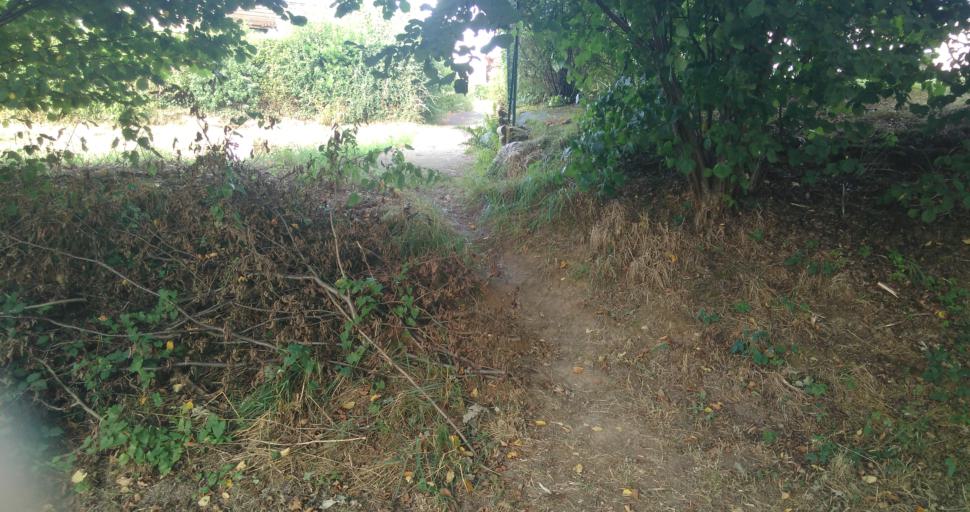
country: FR
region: Brittany
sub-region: Departement d'Ille-et-Vilaine
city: Geveze
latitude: 48.2206
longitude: -1.7809
